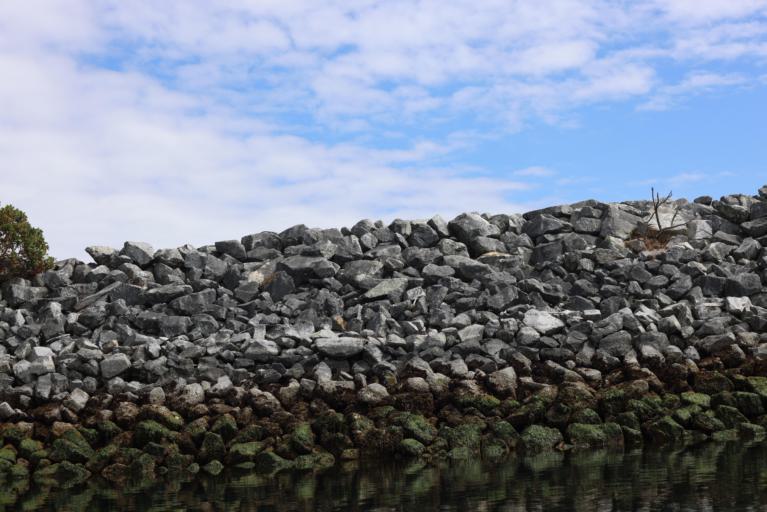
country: CA
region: British Columbia
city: North Saanich
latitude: 48.6529
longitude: -123.3932
